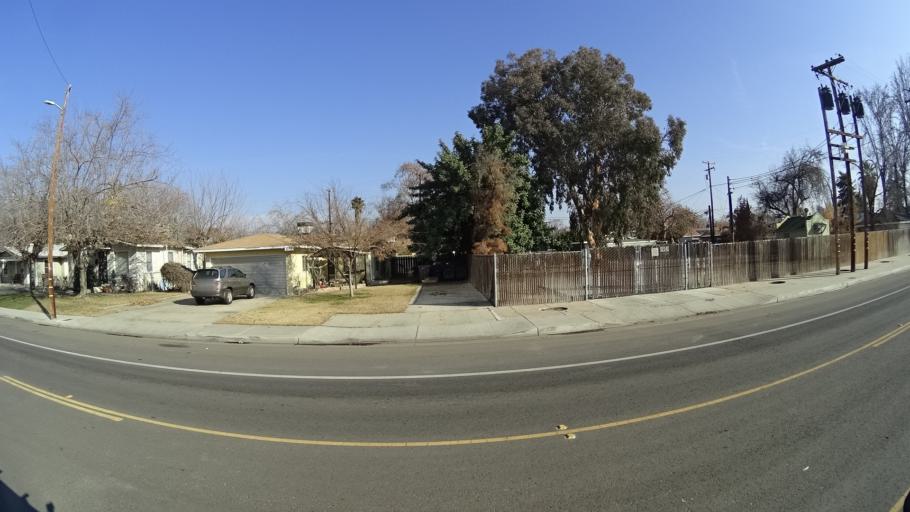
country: US
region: California
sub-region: Kern County
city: Bakersfield
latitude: 35.3589
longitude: -119.0295
